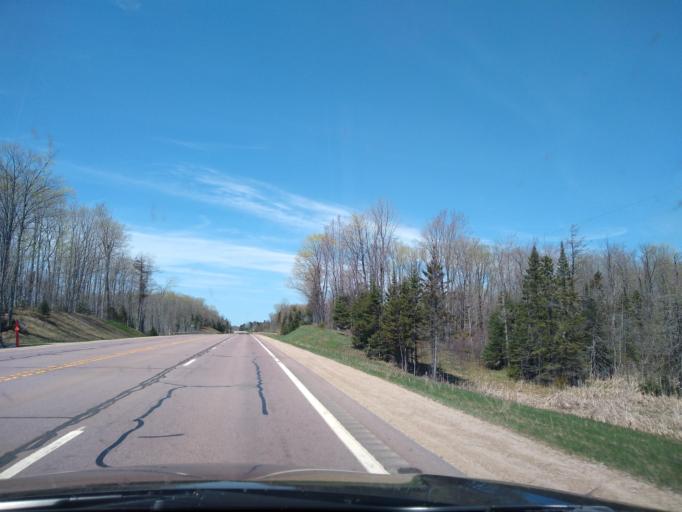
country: US
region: Michigan
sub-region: Marquette County
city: K. I. Sawyer Air Force Base
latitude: 46.2624
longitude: -87.0991
